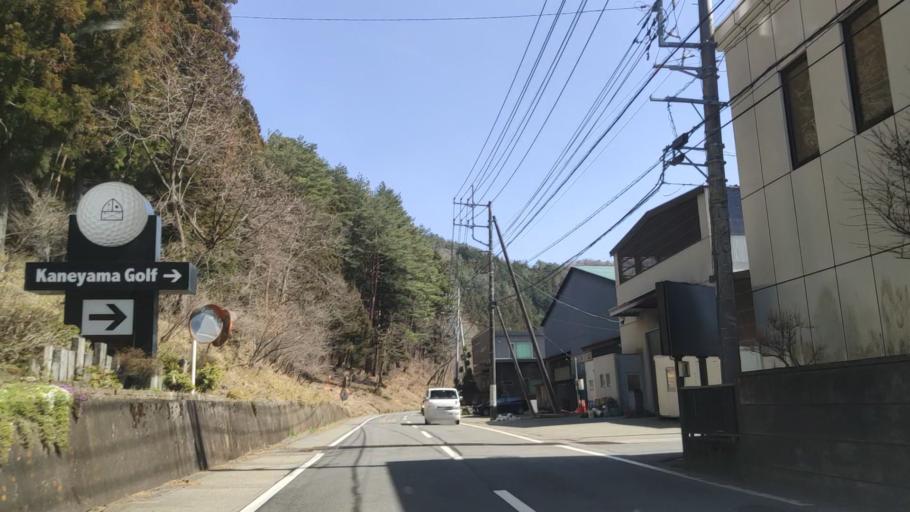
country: JP
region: Yamanashi
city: Fujikawaguchiko
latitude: 35.4637
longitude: 138.8160
